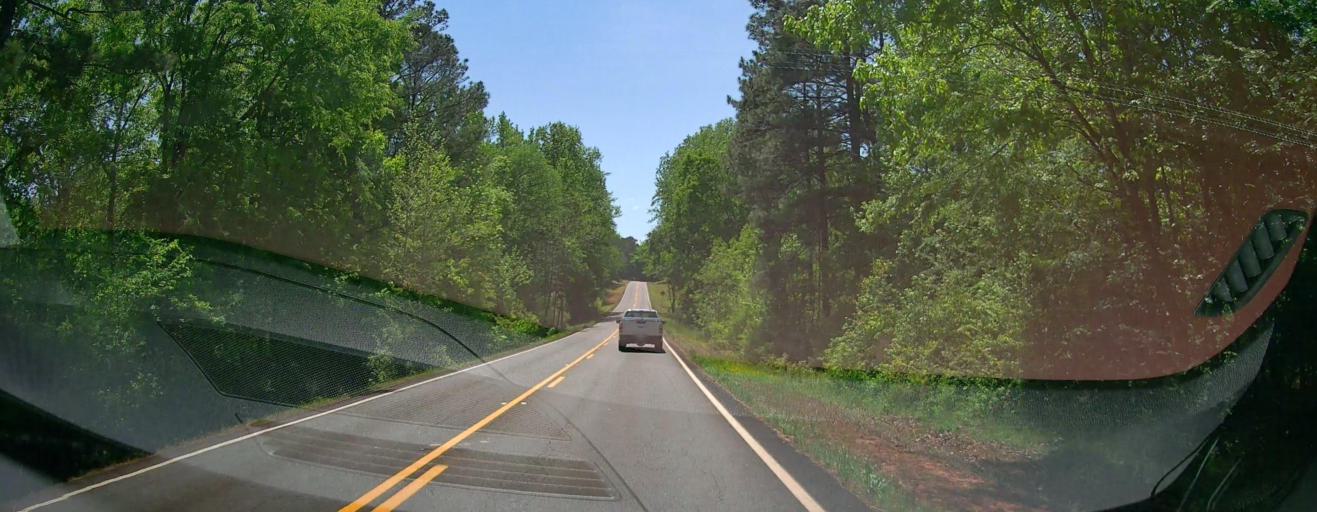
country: US
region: Georgia
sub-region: Jasper County
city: Monticello
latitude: 33.2773
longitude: -83.6553
